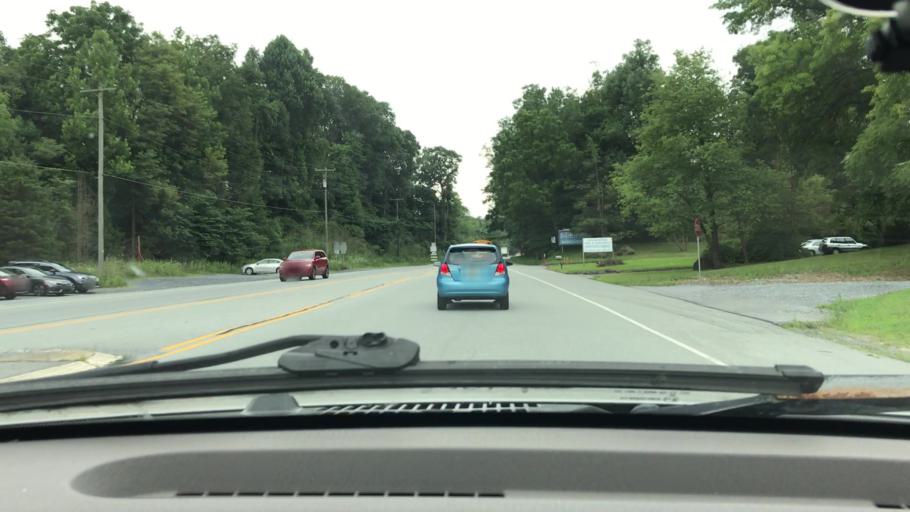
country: US
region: Pennsylvania
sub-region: Lancaster County
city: Elizabethtown
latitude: 40.1760
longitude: -76.6021
